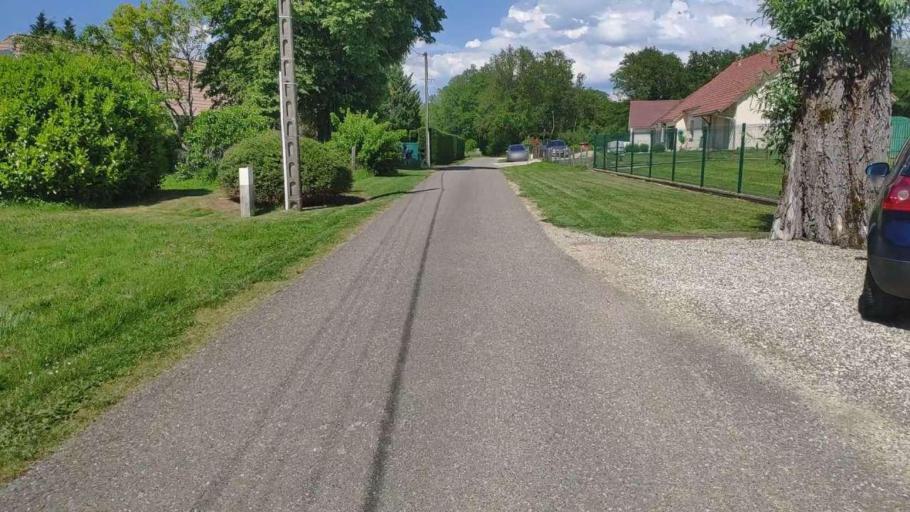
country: FR
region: Franche-Comte
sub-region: Departement du Jura
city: Bletterans
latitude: 46.8000
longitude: 5.4197
